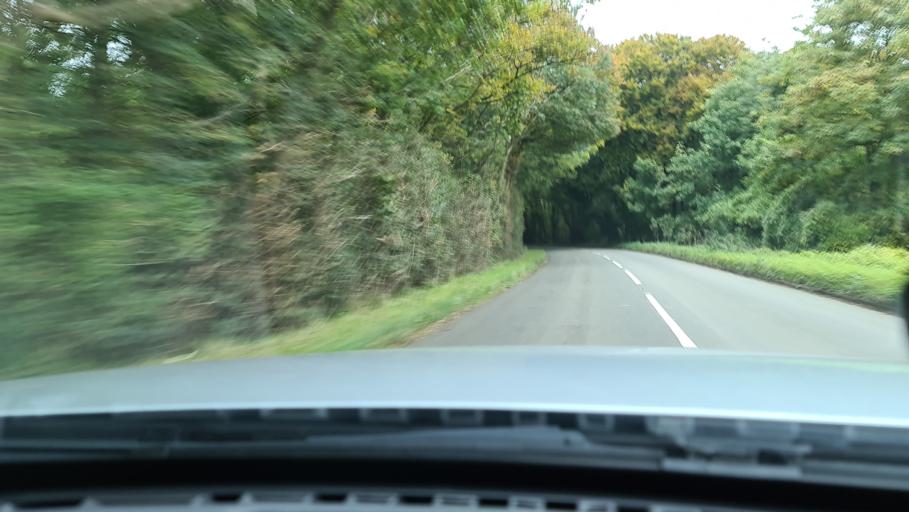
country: GB
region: England
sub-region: Oxfordshire
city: Somerton
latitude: 51.9247
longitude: -1.2414
